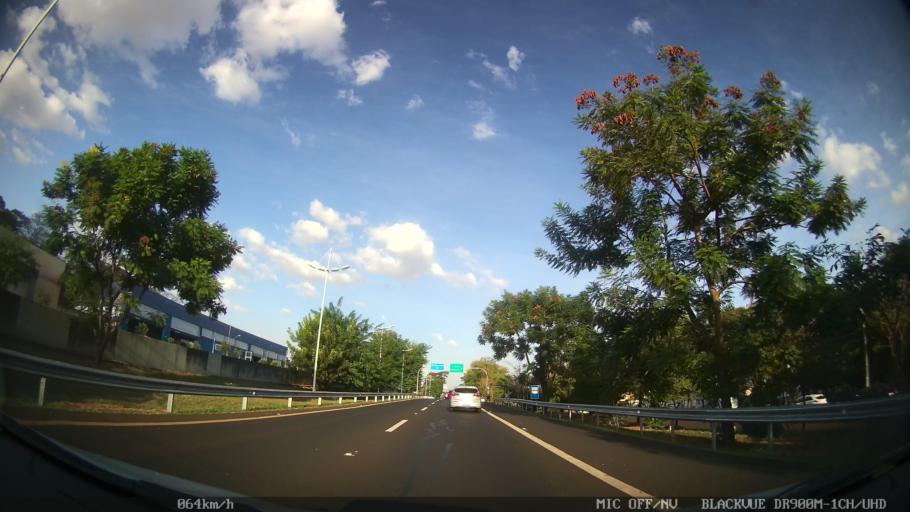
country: BR
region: Sao Paulo
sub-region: Ribeirao Preto
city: Ribeirao Preto
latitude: -21.1899
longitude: -47.7814
